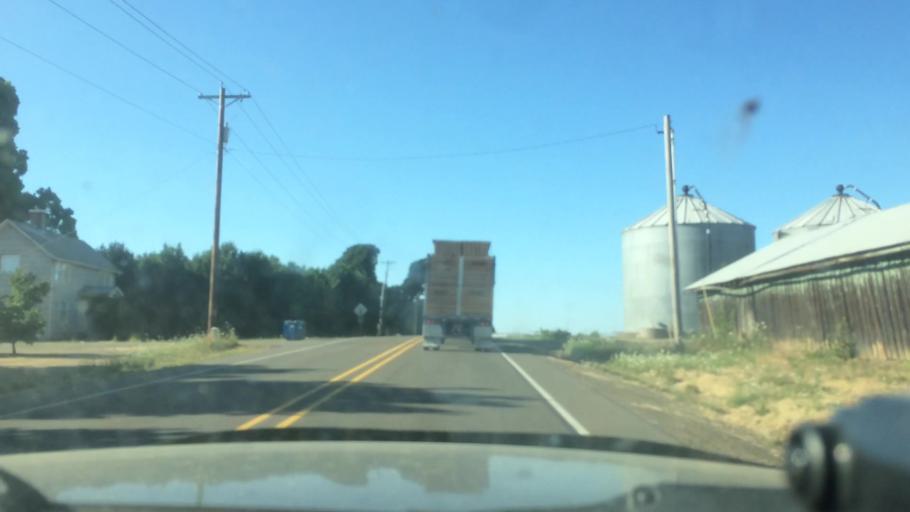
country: US
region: Oregon
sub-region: Marion County
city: Gervais
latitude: 45.0799
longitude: -122.9762
